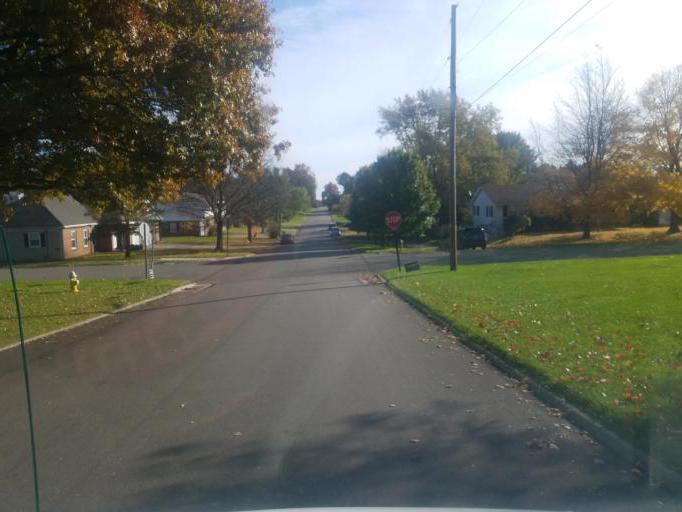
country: US
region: Ohio
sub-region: Richland County
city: Mansfield
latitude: 40.7295
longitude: -82.5293
